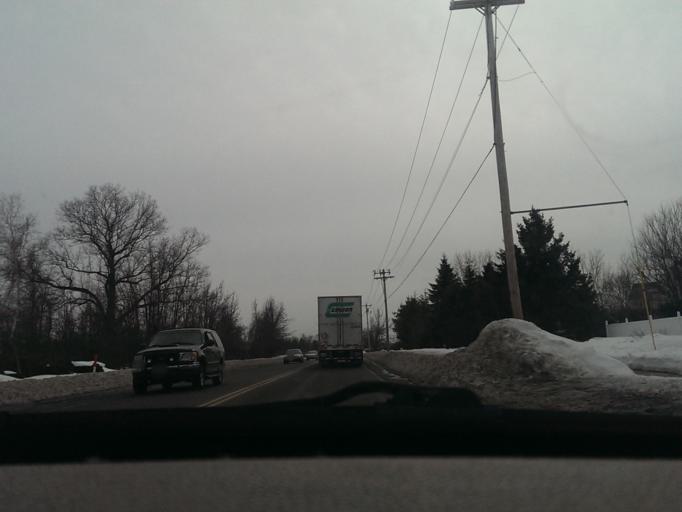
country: US
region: Massachusetts
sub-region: Hampden County
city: East Longmeadow
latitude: 42.0500
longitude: -72.5324
